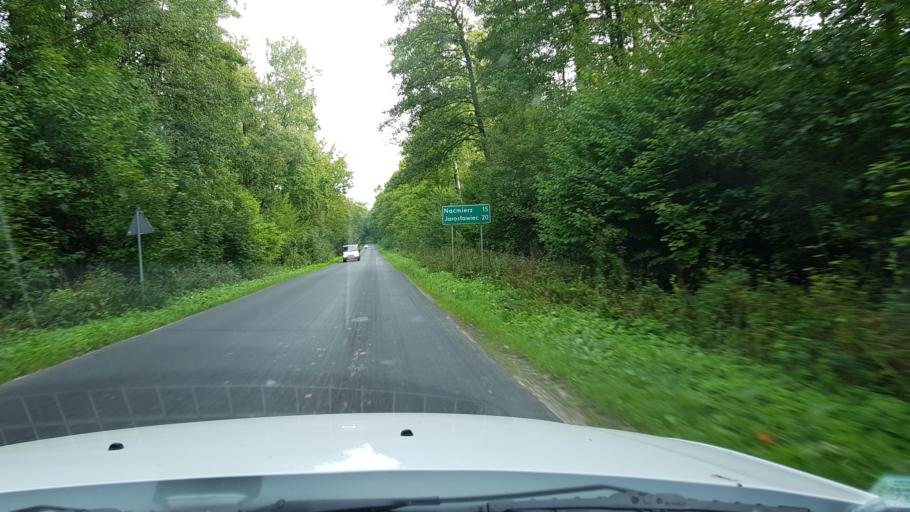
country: PL
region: West Pomeranian Voivodeship
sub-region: Powiat slawienski
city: Slawno
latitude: 54.3892
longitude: 16.6149
